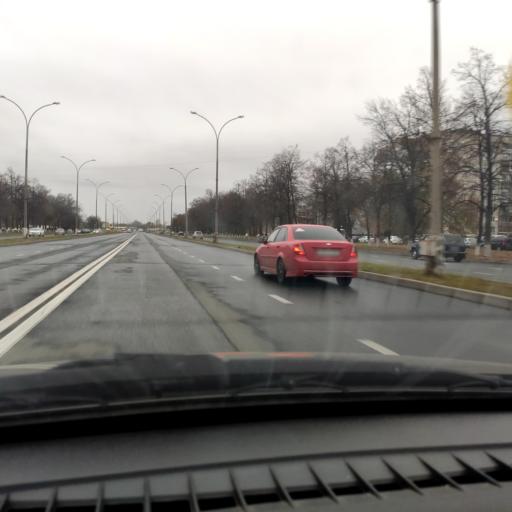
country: RU
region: Samara
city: Tol'yatti
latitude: 53.5299
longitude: 49.2705
